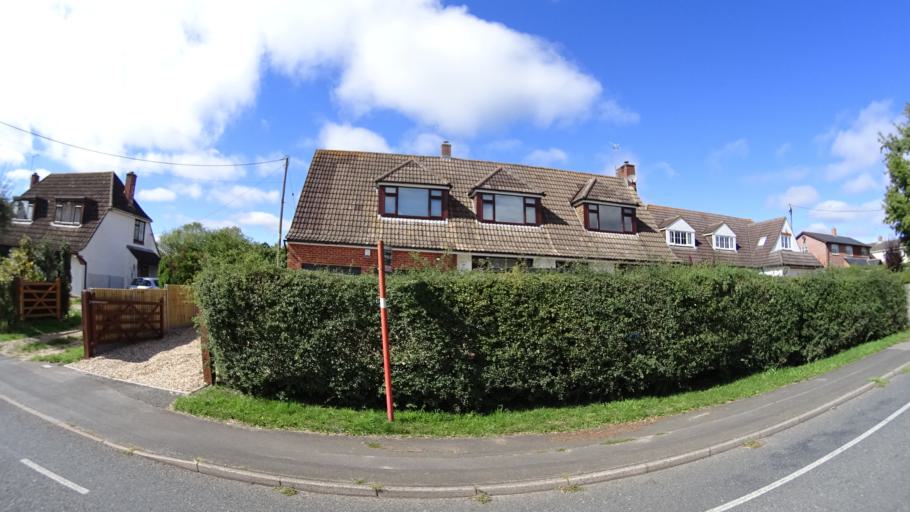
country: GB
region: England
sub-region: Hampshire
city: Romsey
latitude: 51.0162
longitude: -1.4693
